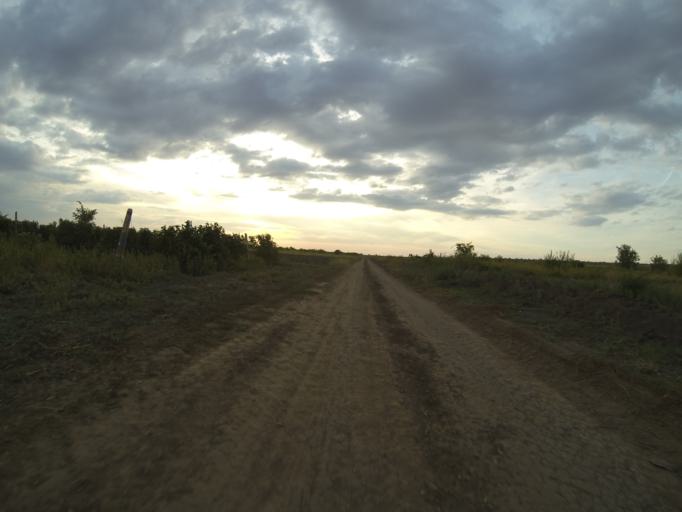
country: RO
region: Dolj
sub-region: Comuna Ceratu
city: Ceratu
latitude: 44.0999
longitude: 23.6791
